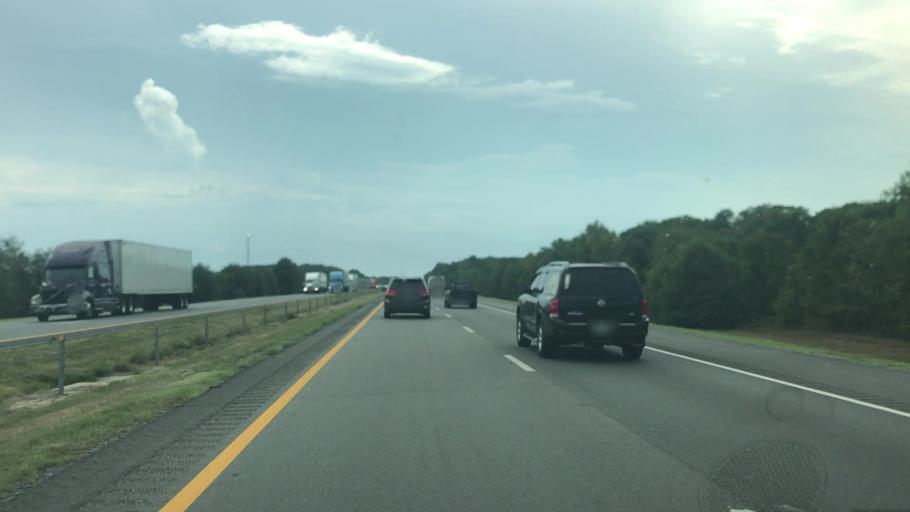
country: US
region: Arkansas
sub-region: Monroe County
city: Brinkley
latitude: 34.8824
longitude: -91.2633
